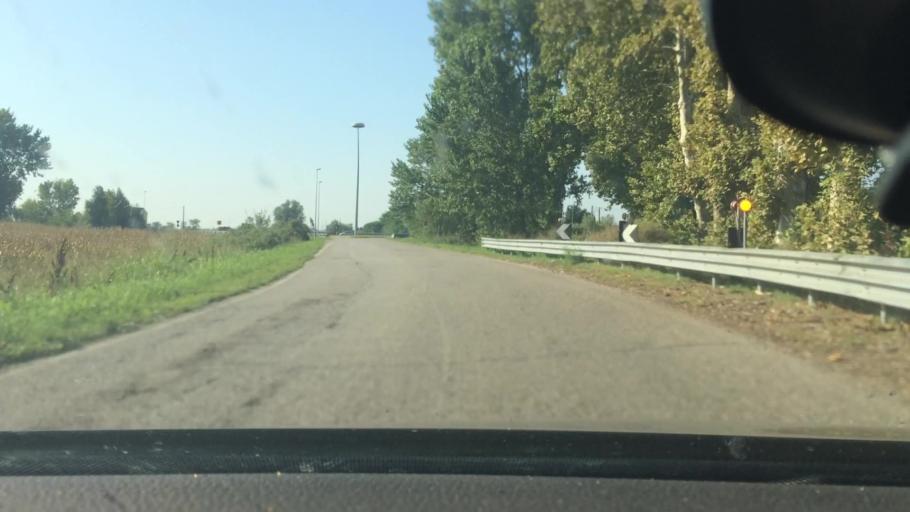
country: IT
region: Emilia-Romagna
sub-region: Provincia di Ferrara
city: Lagosanto
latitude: 44.7485
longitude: 12.1362
